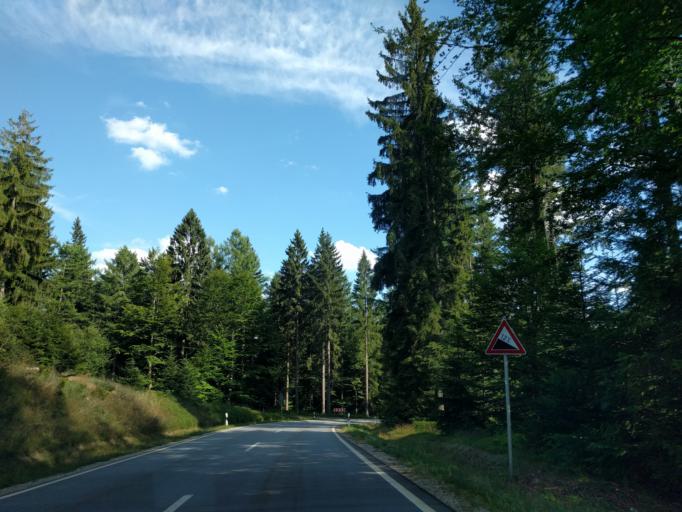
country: DE
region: Bavaria
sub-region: Lower Bavaria
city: Bodenmais
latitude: 49.0653
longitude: 13.1369
